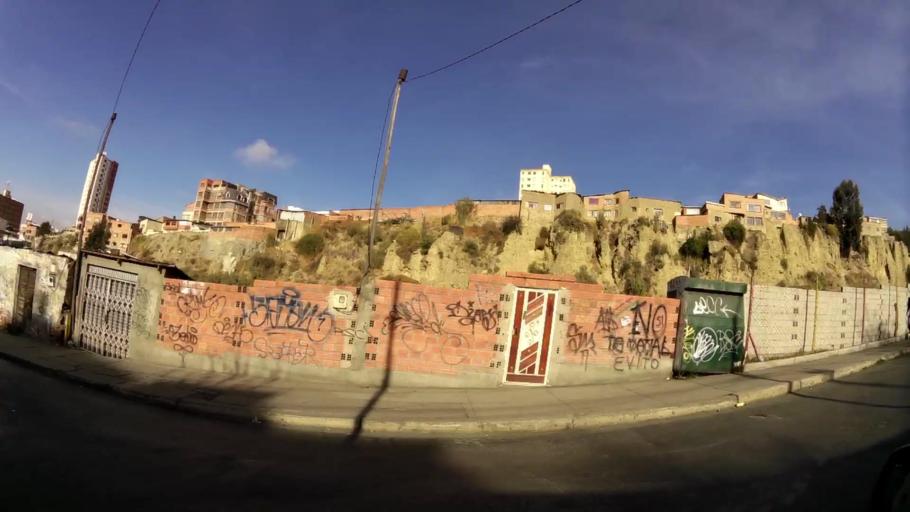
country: BO
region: La Paz
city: La Paz
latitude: -16.4950
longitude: -68.1184
